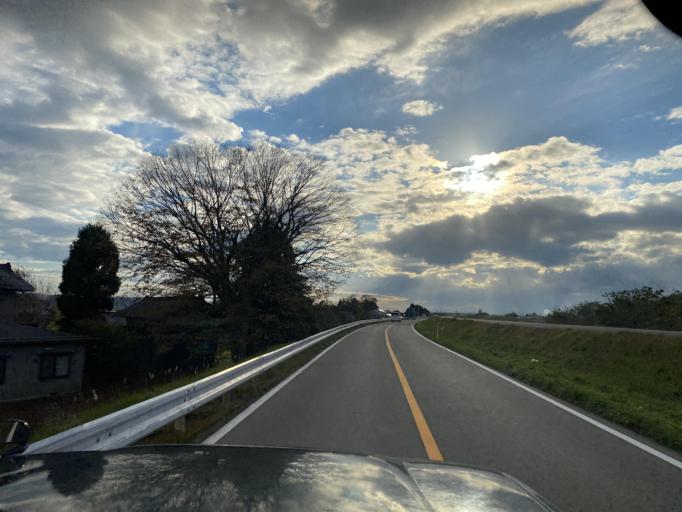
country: JP
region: Niigata
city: Kamo
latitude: 37.6872
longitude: 139.0298
